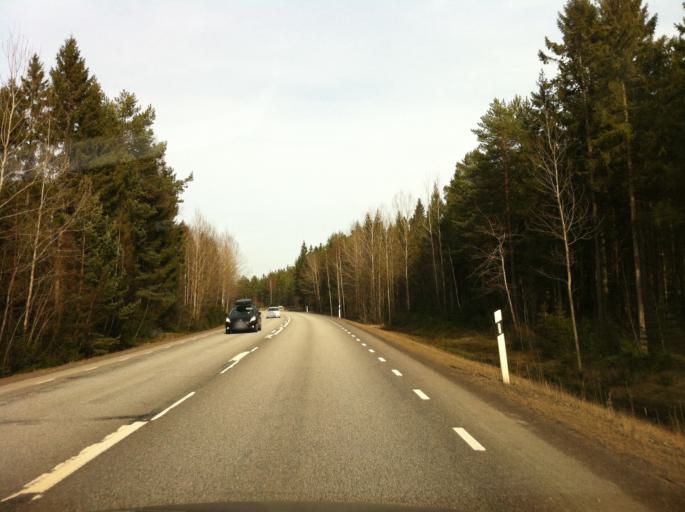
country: SE
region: Vaestra Goetaland
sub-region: Mariestads Kommun
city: Mariestad
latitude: 58.7745
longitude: 13.9570
